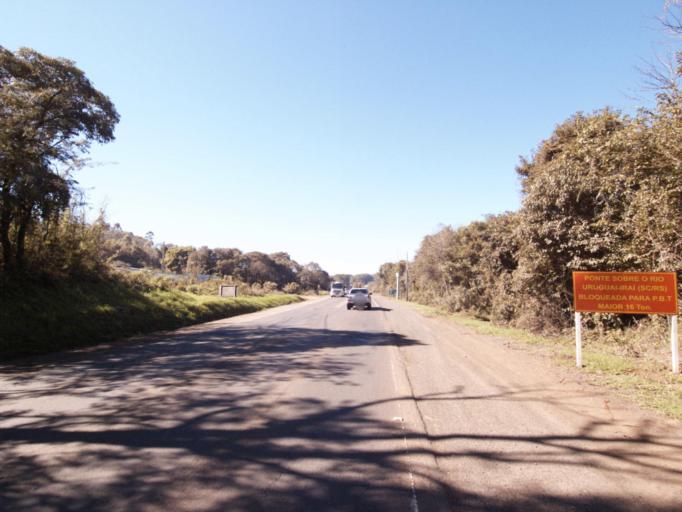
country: BR
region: Santa Catarina
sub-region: Sao Lourenco Do Oeste
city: Sao Lourenco dOeste
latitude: -26.8050
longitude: -53.1835
